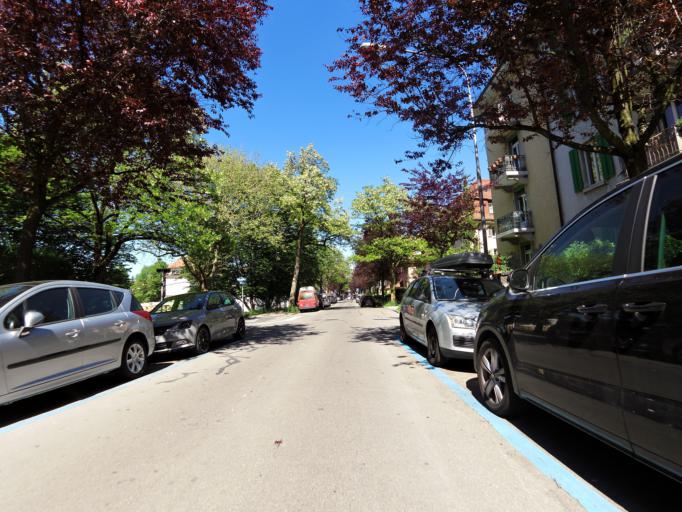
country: CH
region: Zurich
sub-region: Bezirk Zuerich
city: Zuerich (Kreis 3) / Sihlfeld
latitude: 47.3724
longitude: 8.5108
